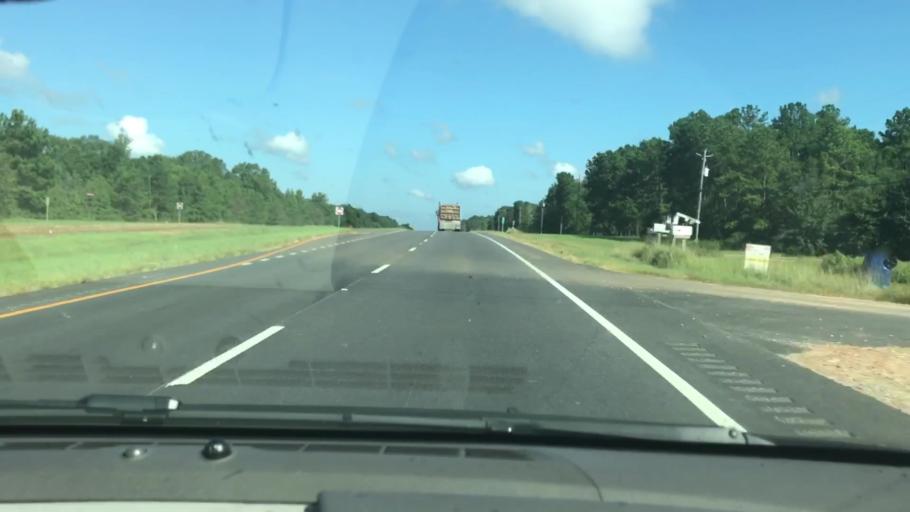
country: US
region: Alabama
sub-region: Barbour County
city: Eufaula
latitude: 32.0290
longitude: -85.1209
